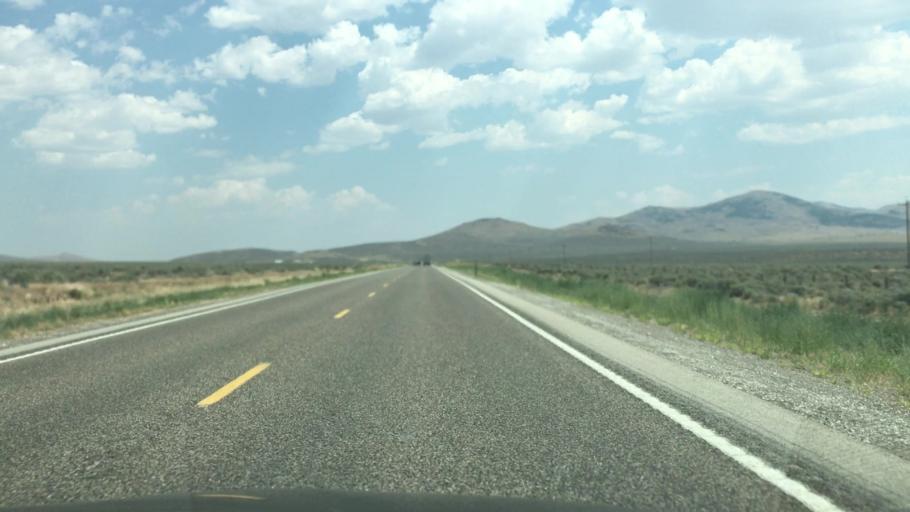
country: US
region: Nevada
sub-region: Elko County
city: Wells
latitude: 41.1608
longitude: -114.8929
